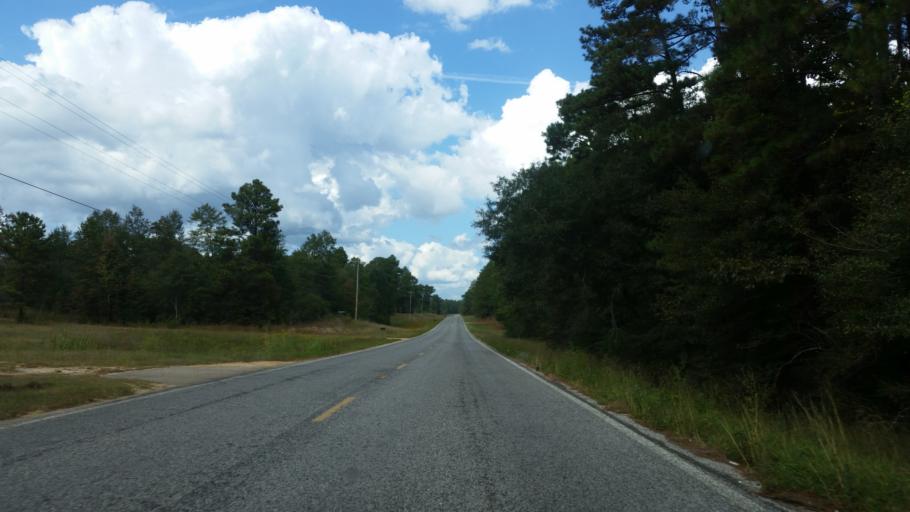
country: US
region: Mississippi
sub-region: Stone County
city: Wiggins
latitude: 30.8890
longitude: -89.1168
